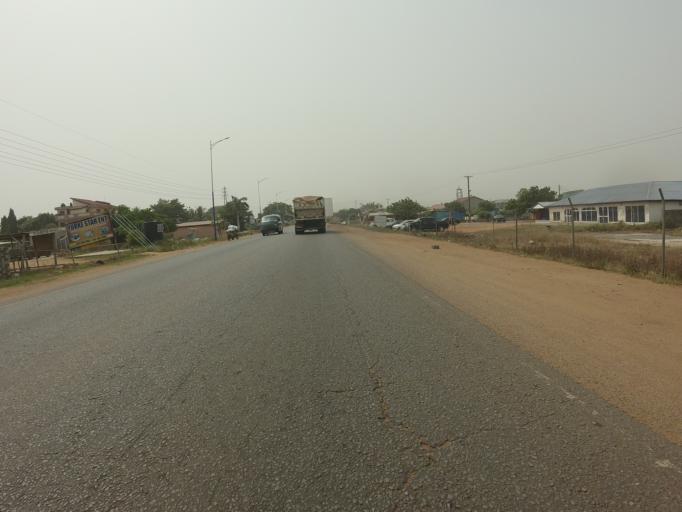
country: GH
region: Greater Accra
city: Tema
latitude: 5.7527
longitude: 0.0450
